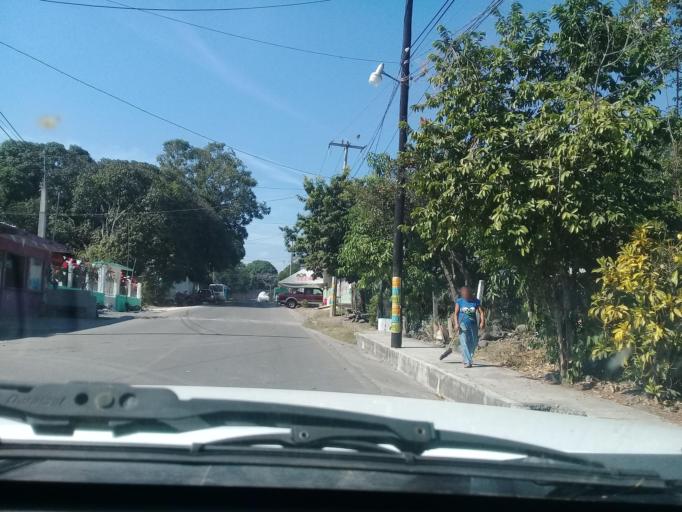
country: MX
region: Veracruz
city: Actopan
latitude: 19.4752
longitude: -96.5772
